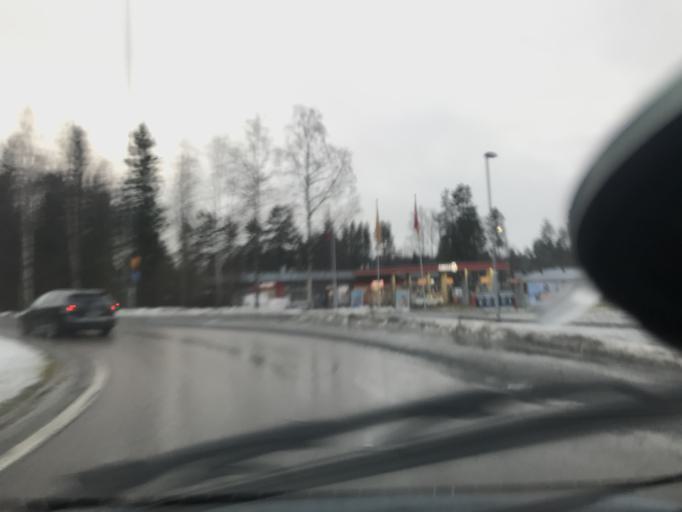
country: SE
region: Norrbotten
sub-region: Lulea Kommun
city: Gammelstad
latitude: 65.6333
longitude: 22.0325
